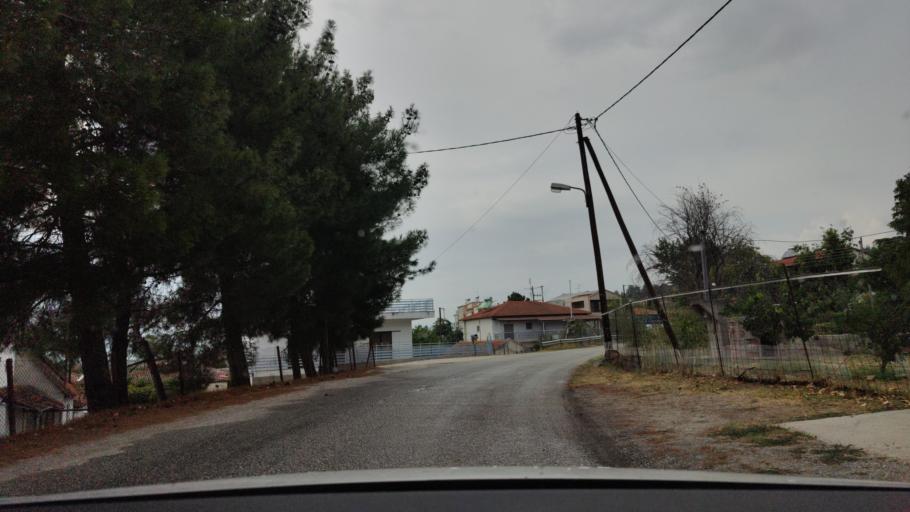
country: GR
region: Central Macedonia
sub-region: Nomos Serron
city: Lefkonas
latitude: 41.1186
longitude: 23.4609
